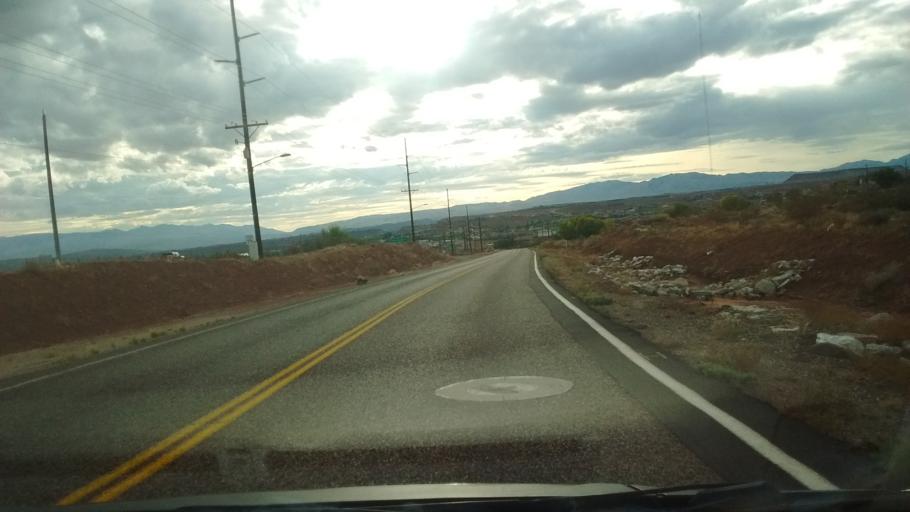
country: US
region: Utah
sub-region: Washington County
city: Washington
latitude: 37.1434
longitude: -113.5009
